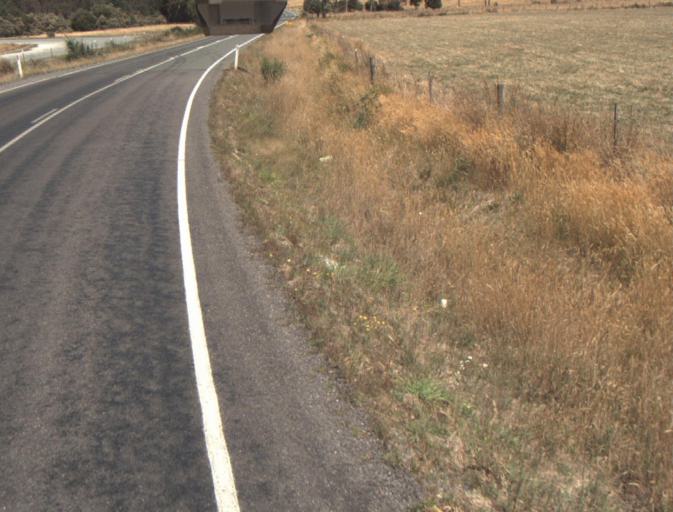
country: AU
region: Tasmania
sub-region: Launceston
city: Newstead
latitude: -41.3298
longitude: 147.3533
